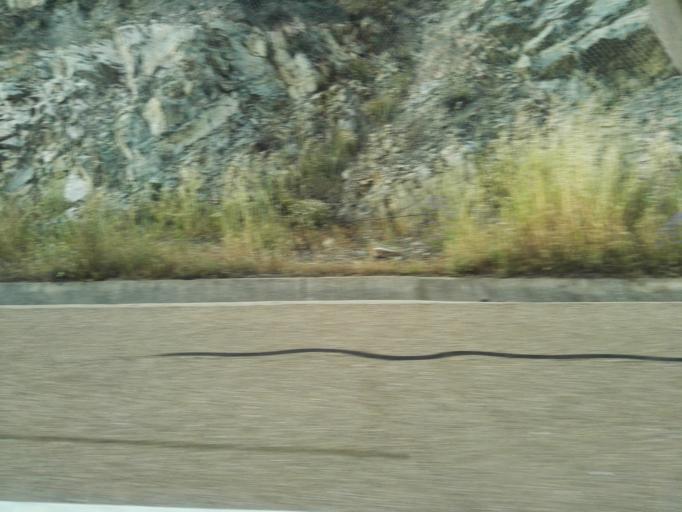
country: PT
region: Portalegre
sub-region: Elvas
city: Elvas
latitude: 38.9023
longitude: -7.1391
